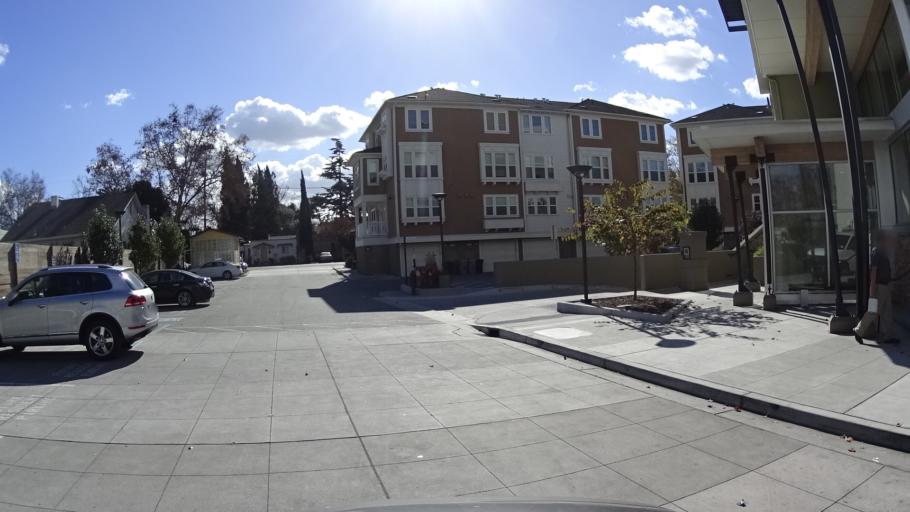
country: US
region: California
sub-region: Santa Clara County
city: San Jose
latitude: 37.3341
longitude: -121.9080
